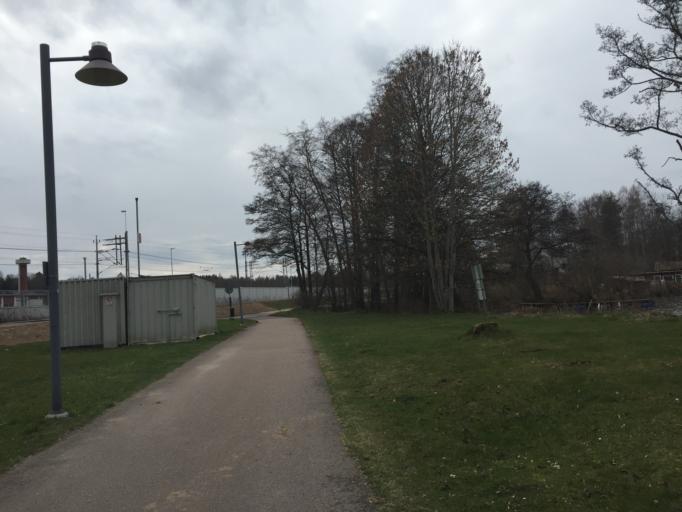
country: SE
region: OEstergoetland
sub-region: Motala Kommun
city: Motala
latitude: 58.5297
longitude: 15.0372
